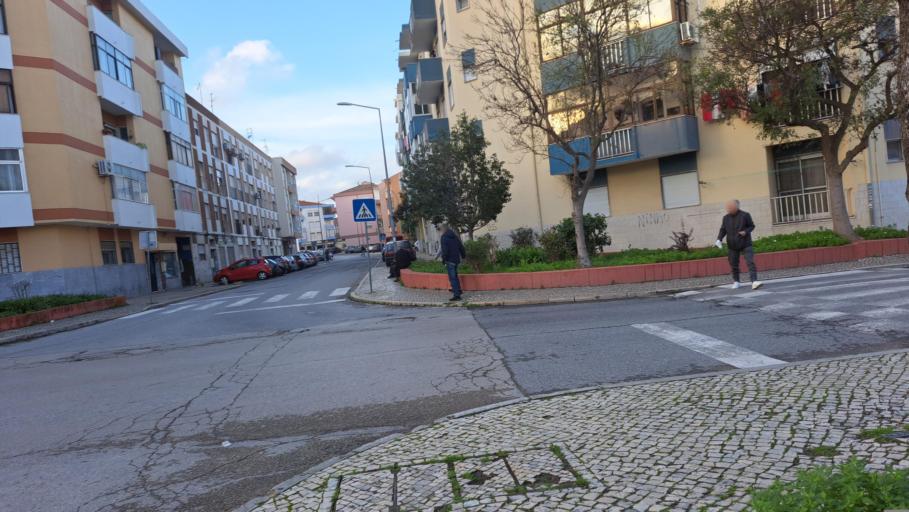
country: PT
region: Setubal
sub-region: Moita
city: Alhos Vedros
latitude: 38.6543
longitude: -9.0416
